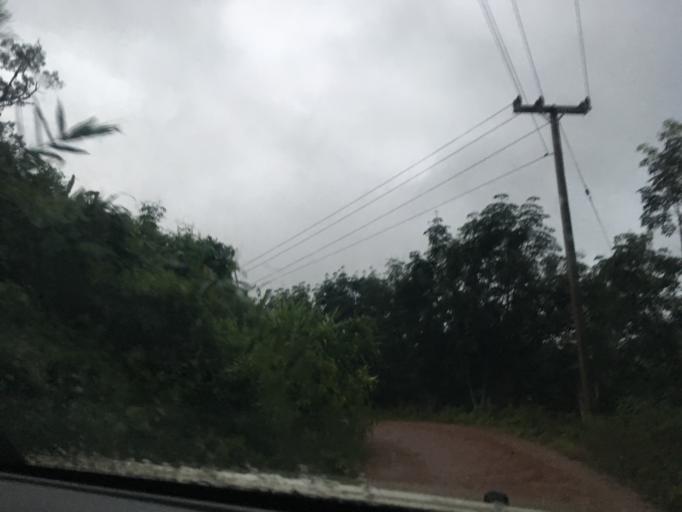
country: LA
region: Oudomxai
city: Muang La
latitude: 21.2541
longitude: 101.9322
